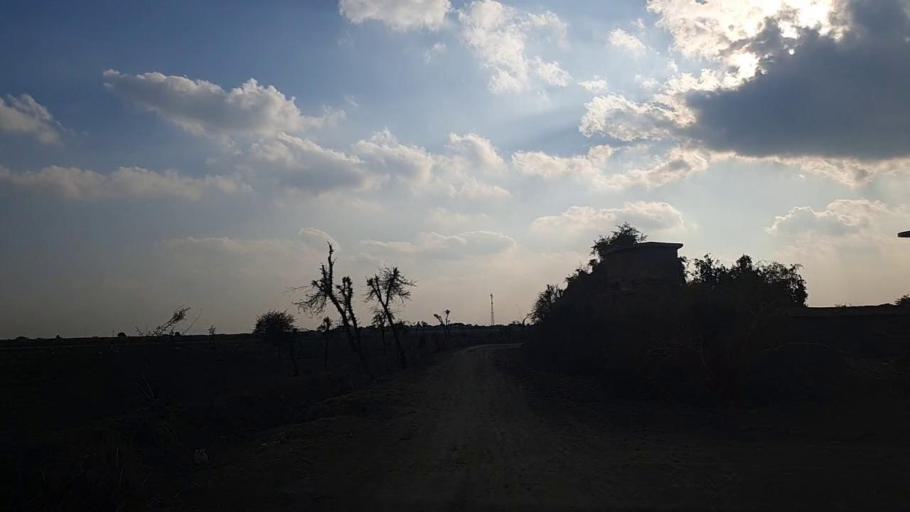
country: PK
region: Sindh
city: Tando Mittha Khan
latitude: 25.9429
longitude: 69.2497
